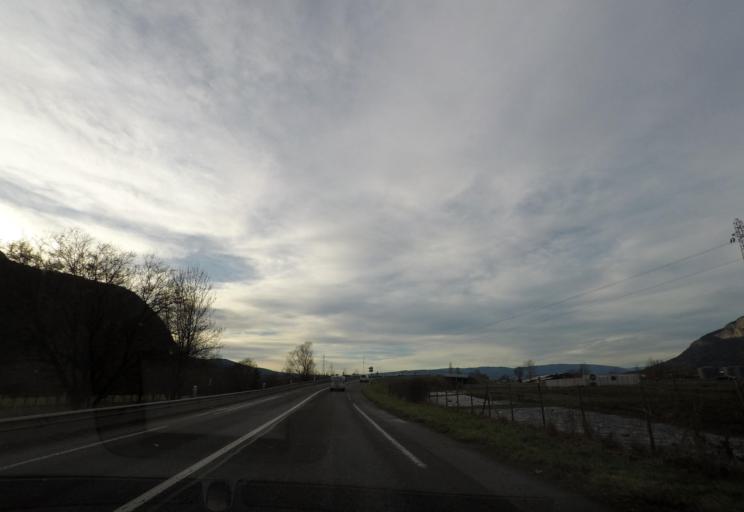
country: FR
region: Rhone-Alpes
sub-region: Departement de la Haute-Savoie
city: Ayse
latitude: 46.0700
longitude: 6.4346
